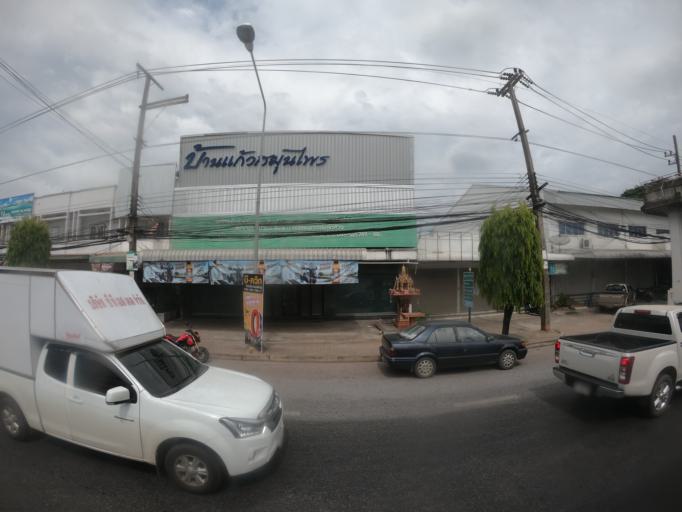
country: TH
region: Roi Et
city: Roi Et
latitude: 16.0552
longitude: 103.6400
